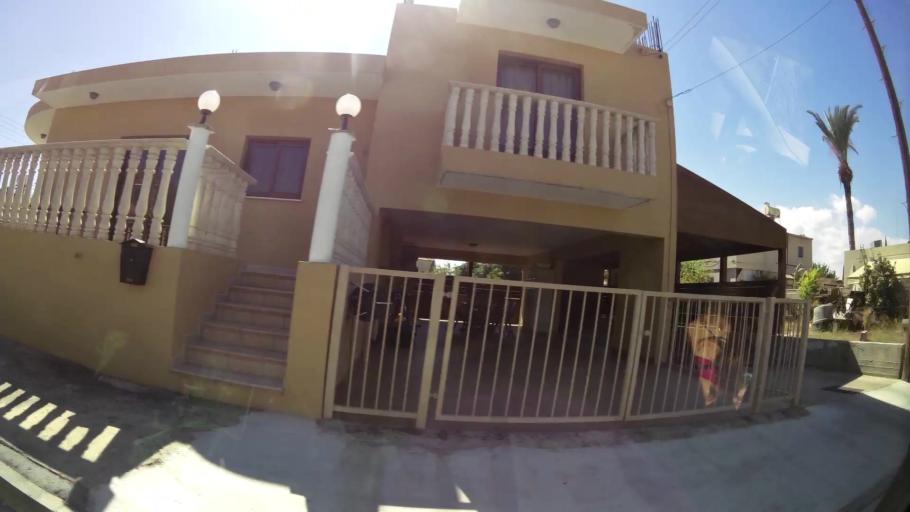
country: CY
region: Larnaka
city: Livadia
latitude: 34.9541
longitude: 33.6296
